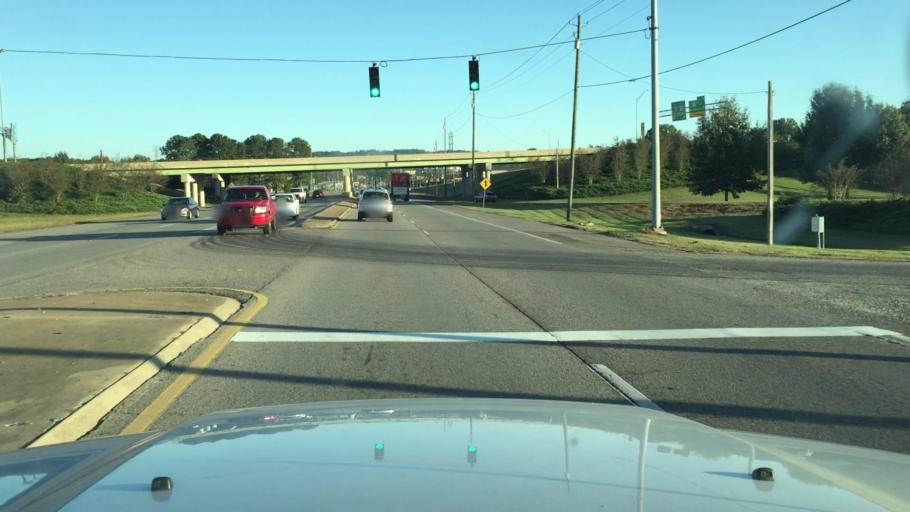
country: US
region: Alabama
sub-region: Etowah County
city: Gadsden
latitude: 33.9912
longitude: -86.0043
